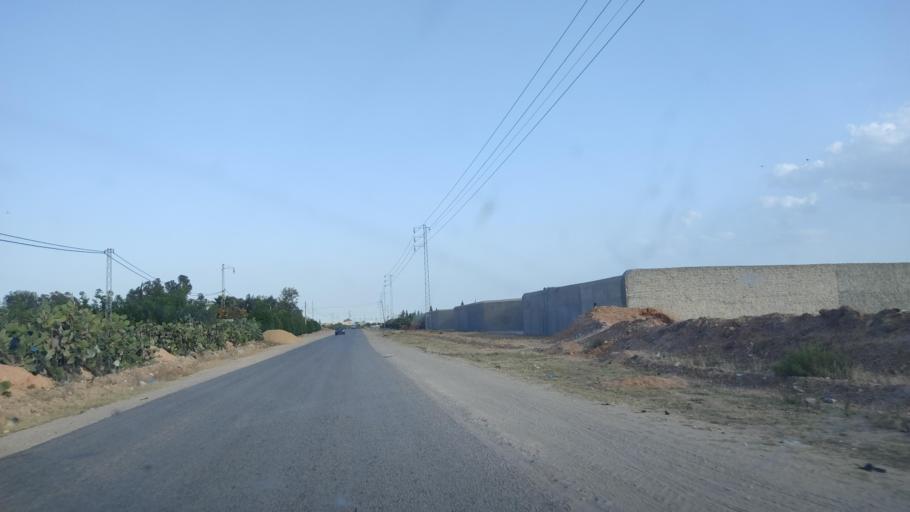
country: TN
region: Safaqis
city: Sfax
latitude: 34.8088
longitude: 10.6649
